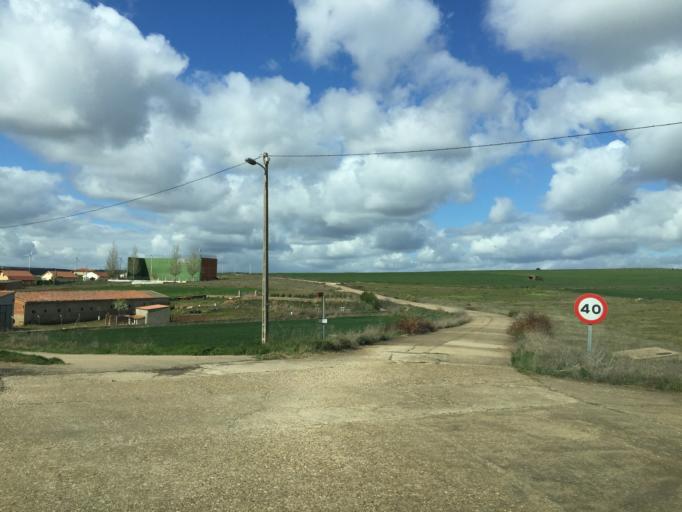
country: ES
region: Castille and Leon
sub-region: Provincia de Zamora
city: Manzanal del Barco
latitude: 41.5865
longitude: -5.9600
